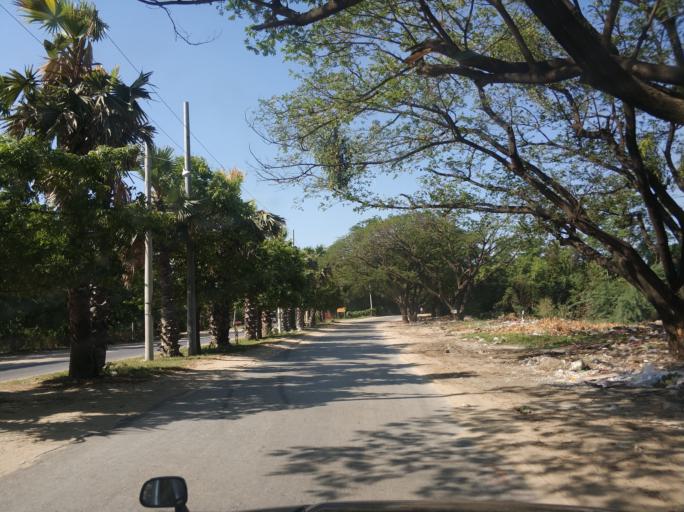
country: MM
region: Mandalay
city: Mandalay
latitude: 21.9564
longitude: 96.0522
